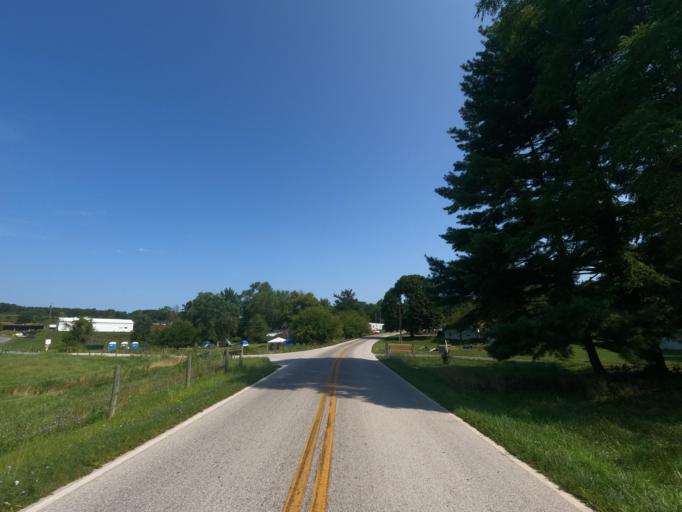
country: US
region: Maryland
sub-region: Carroll County
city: Westminster
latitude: 39.6032
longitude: -77.0105
